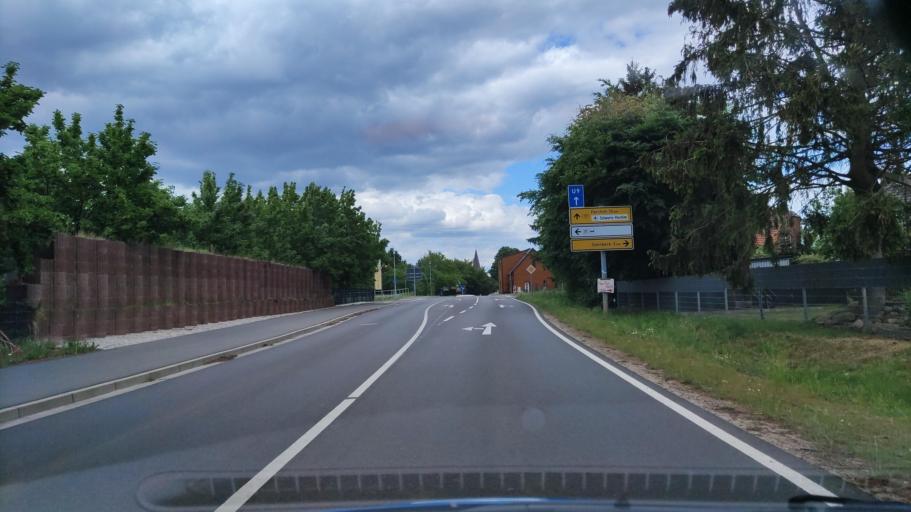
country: DE
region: Mecklenburg-Vorpommern
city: Spornitz
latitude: 53.4046
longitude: 11.7116
